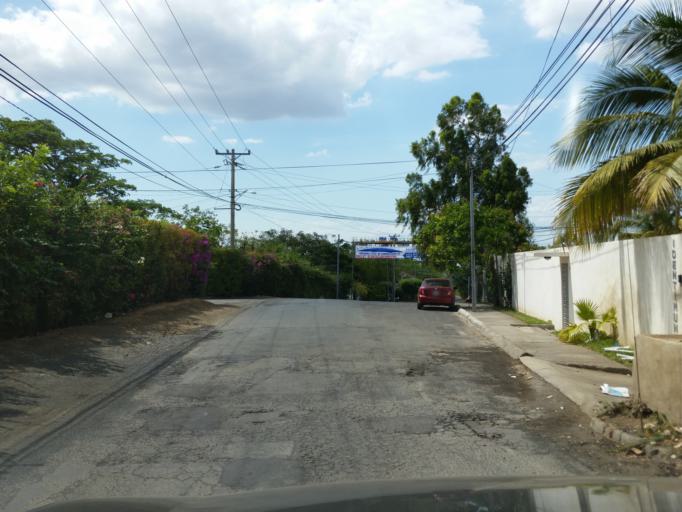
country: NI
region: Managua
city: Managua
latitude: 12.0980
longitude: -86.2576
